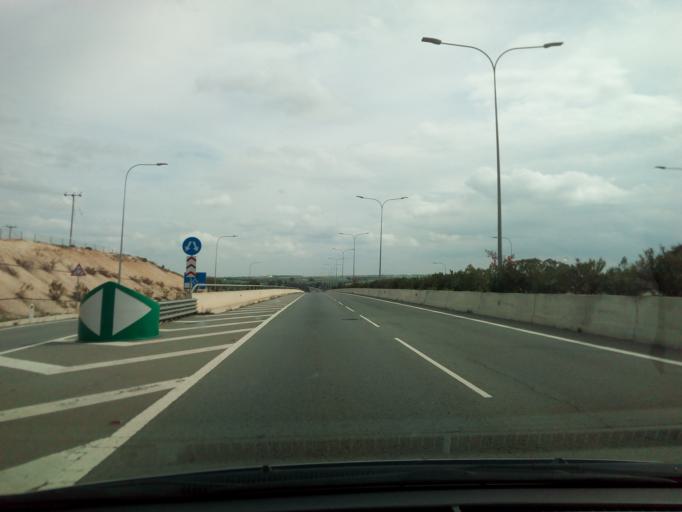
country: CY
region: Lefkosia
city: Kokkinotrimithia
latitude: 35.1512
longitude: 33.2384
